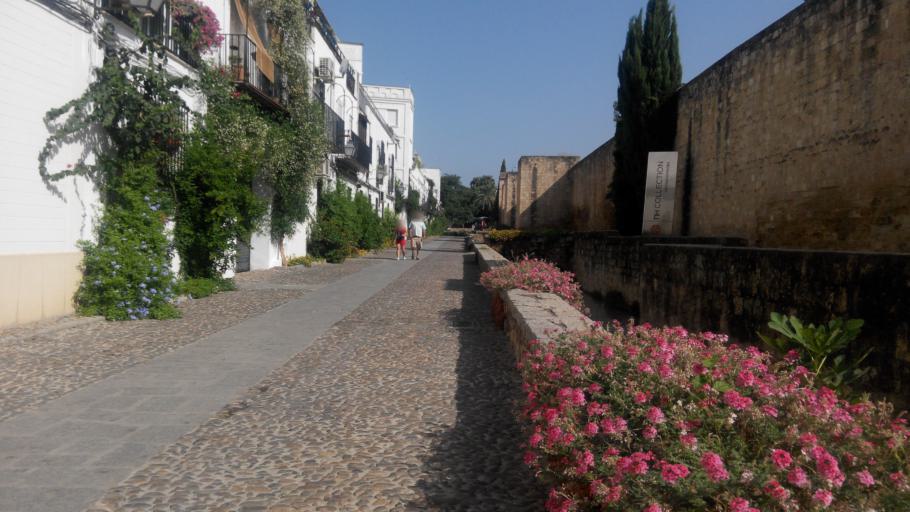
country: ES
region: Andalusia
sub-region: Province of Cordoba
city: Cordoba
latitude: 37.8788
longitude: -4.7833
